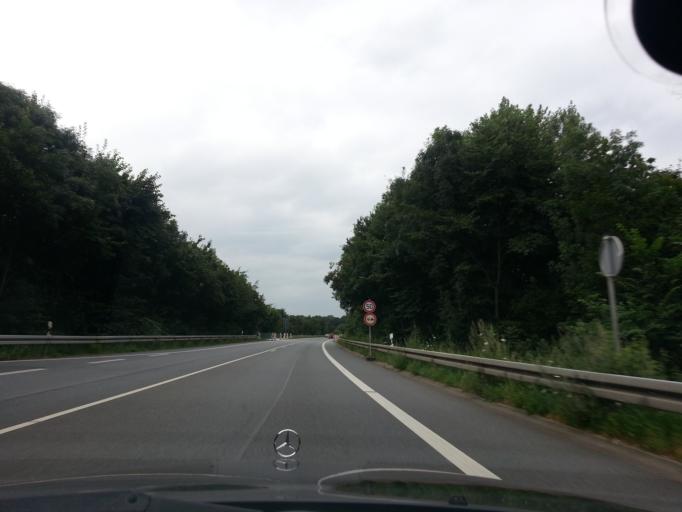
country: DE
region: North Rhine-Westphalia
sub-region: Regierungsbezirk Munster
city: Borken
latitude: 51.8431
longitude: 6.8351
